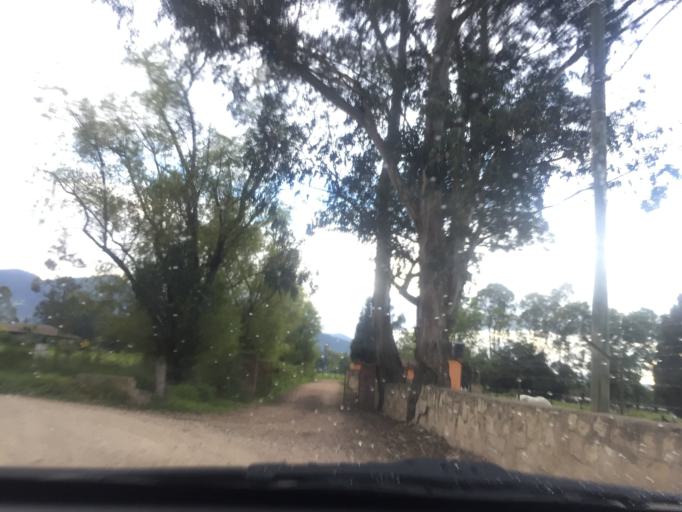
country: CO
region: Cundinamarca
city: Cogua
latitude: 5.0660
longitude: -73.9311
